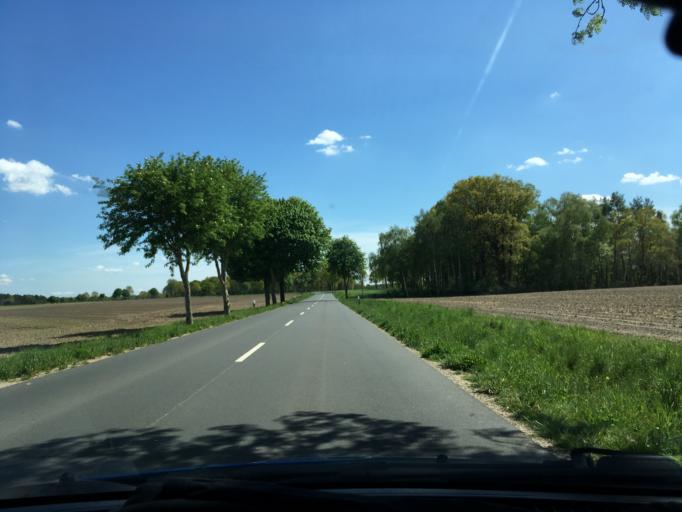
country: DE
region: Lower Saxony
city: Himbergen
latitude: 53.0833
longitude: 10.7463
